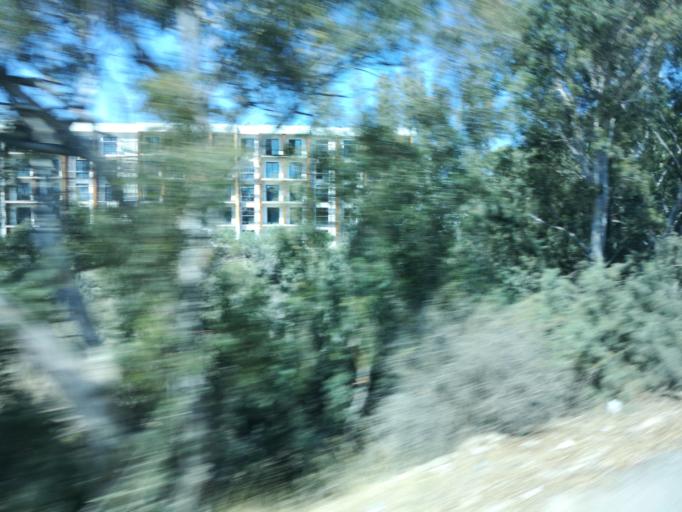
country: CY
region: Ammochostos
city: Famagusta
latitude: 35.1400
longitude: 33.9090
